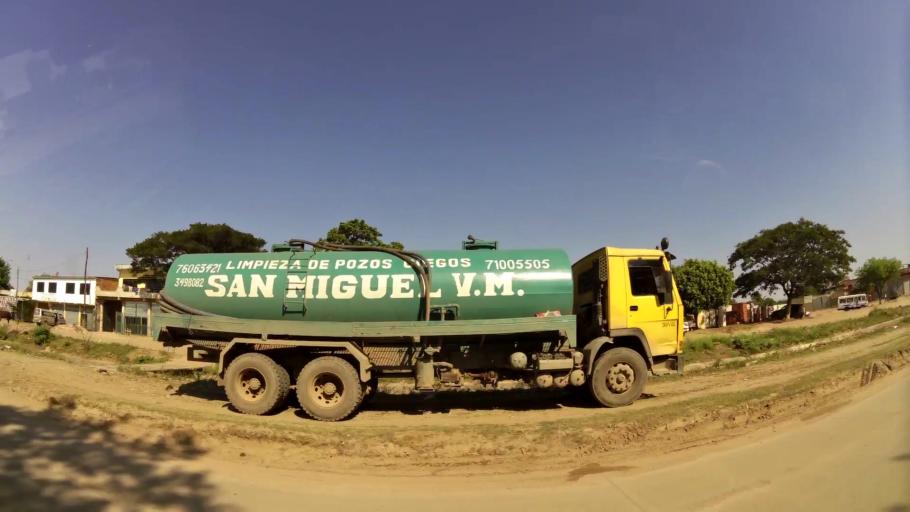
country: BO
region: Santa Cruz
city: Cotoca
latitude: -17.8159
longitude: -63.1139
